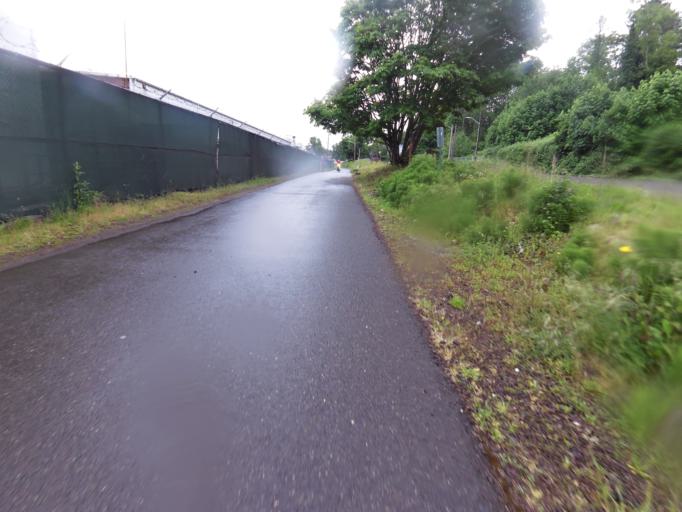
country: US
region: Washington
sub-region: King County
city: Seattle
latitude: 47.6543
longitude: -122.3689
